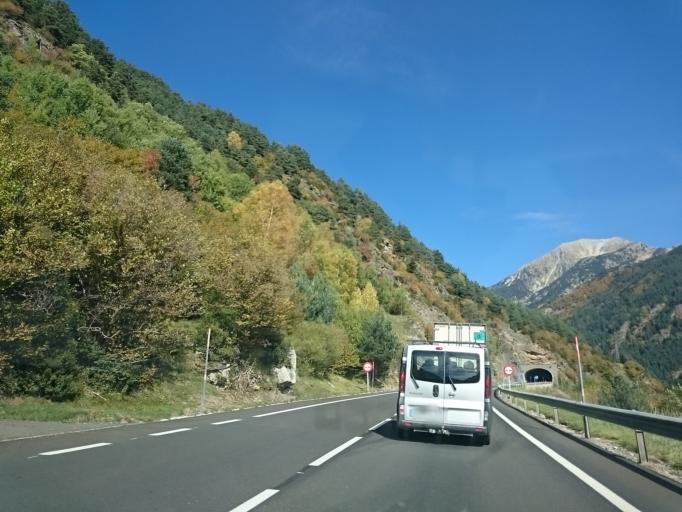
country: ES
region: Catalonia
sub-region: Provincia de Lleida
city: Vielha
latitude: 42.5659
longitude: 0.7511
